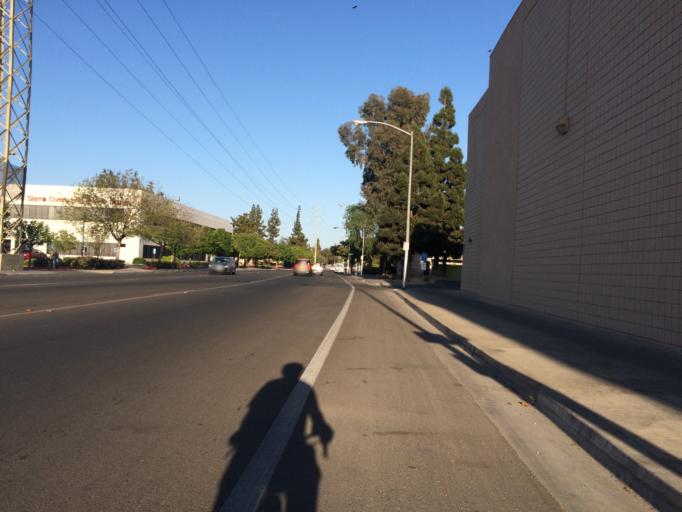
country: US
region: California
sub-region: Fresno County
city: Fresno
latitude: 36.7867
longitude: -119.7890
